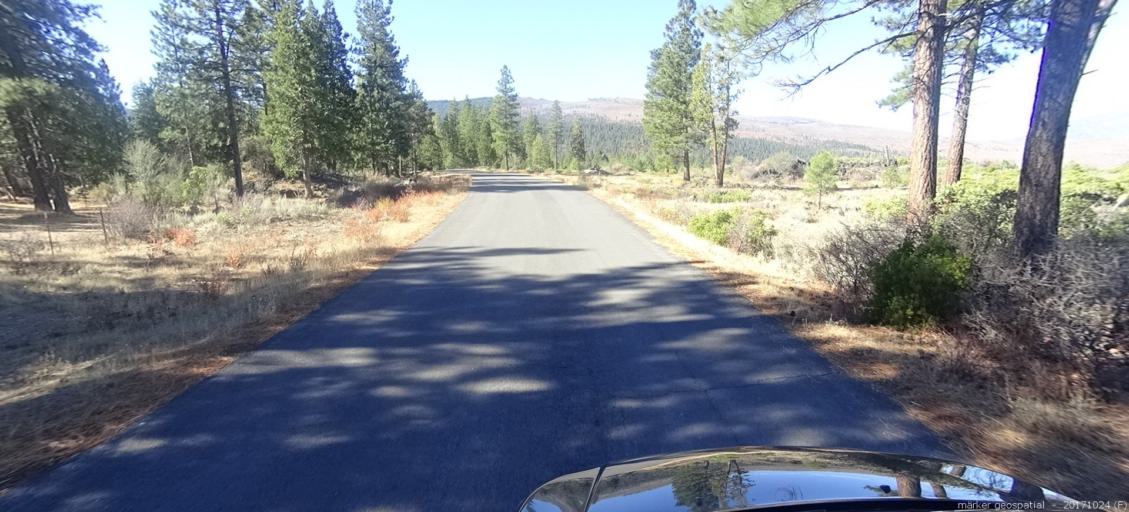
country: US
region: California
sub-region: Shasta County
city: Burney
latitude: 40.7504
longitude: -121.4639
